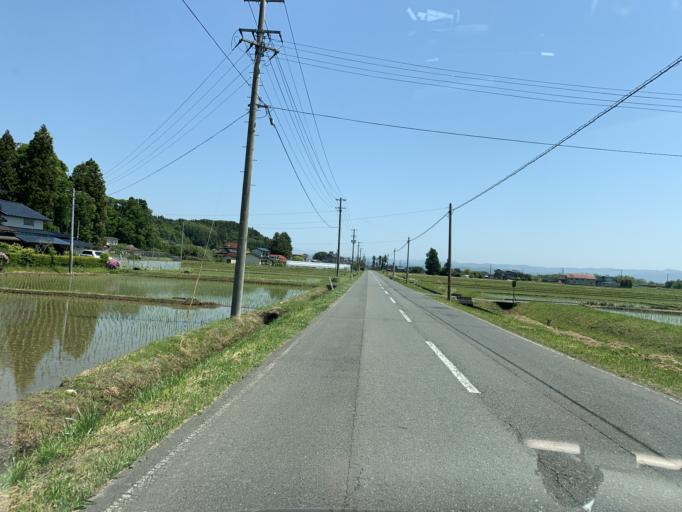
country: JP
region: Iwate
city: Mizusawa
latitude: 39.1648
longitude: 141.0806
